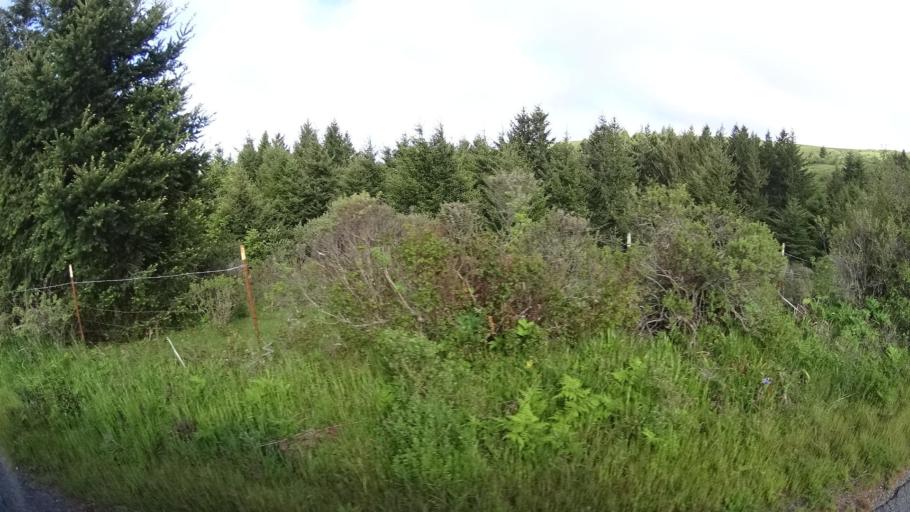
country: US
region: California
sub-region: Humboldt County
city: Ferndale
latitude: 40.4830
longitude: -124.3398
